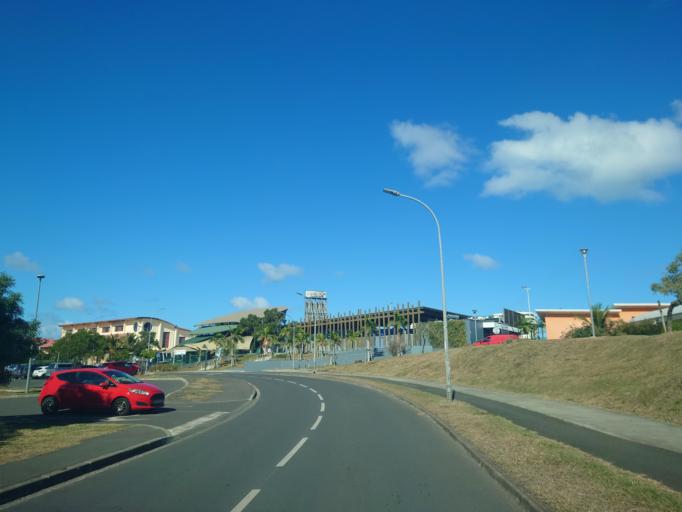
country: NC
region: South Province
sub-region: Noumea
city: Noumea
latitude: -22.2685
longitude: 166.4689
